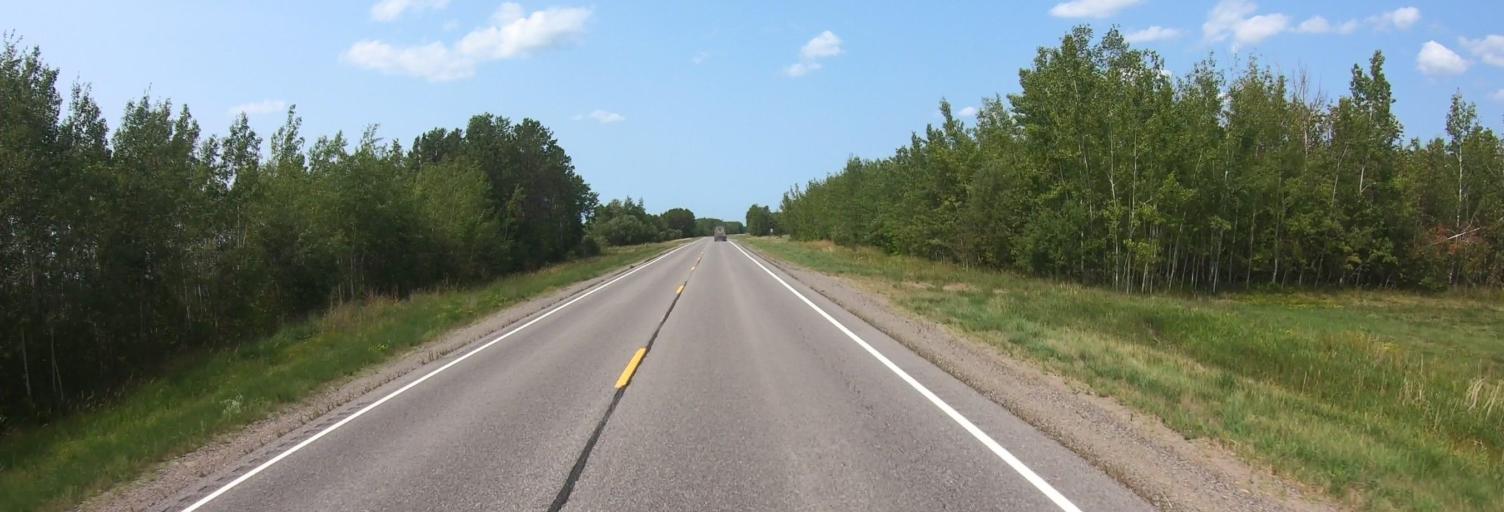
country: US
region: Minnesota
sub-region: Lake of the Woods County
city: Baudette
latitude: 48.6338
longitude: -94.1216
